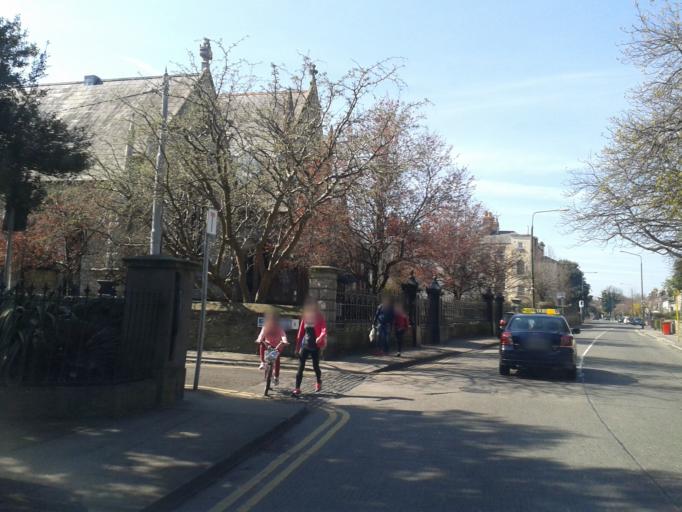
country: IE
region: Leinster
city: Rathmines
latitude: 53.3239
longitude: -6.2586
